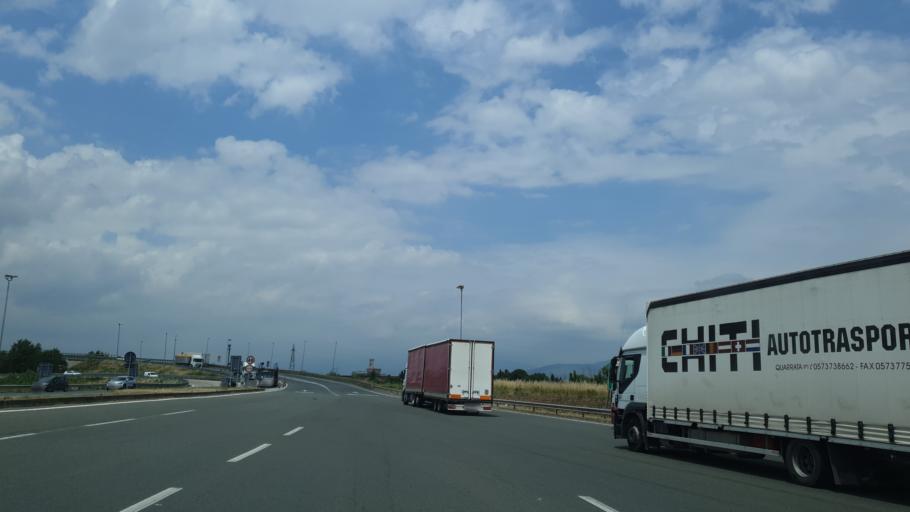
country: IT
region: Tuscany
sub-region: Province of Florence
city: Mantignano-Ugnano
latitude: 43.7764
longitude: 11.1643
